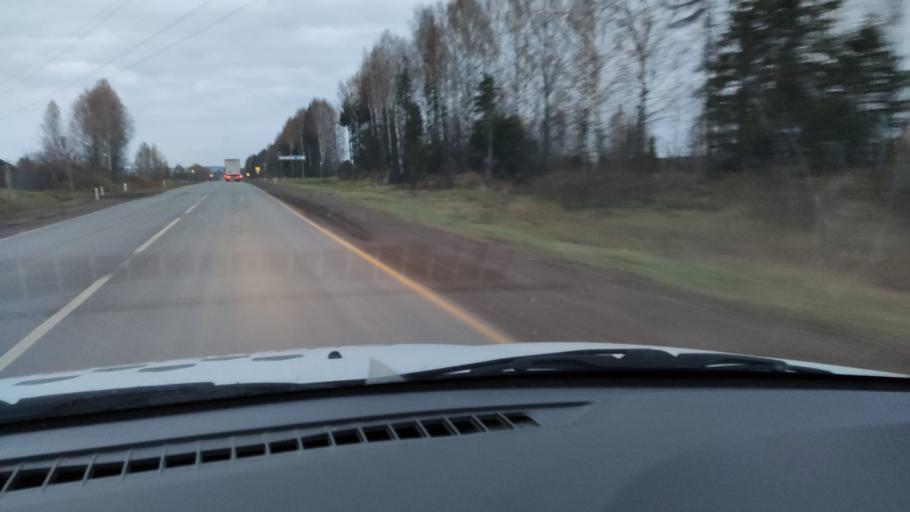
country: RU
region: Kirov
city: Kostino
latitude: 58.8587
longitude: 53.1799
